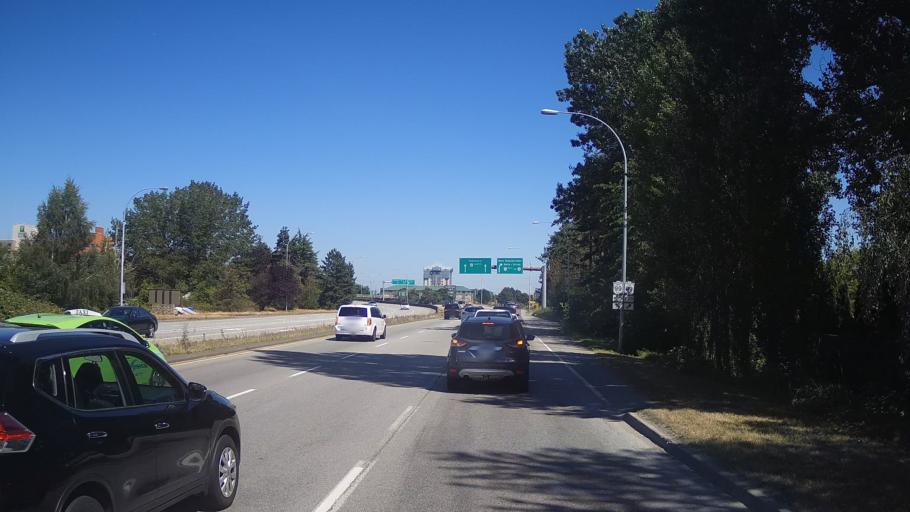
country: CA
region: British Columbia
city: Richmond
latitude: 49.1910
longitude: -123.1234
